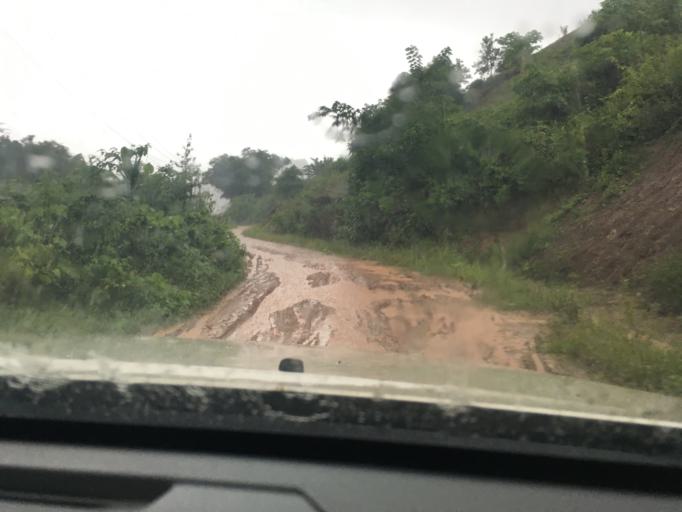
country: LA
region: Oudomxai
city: Muang La
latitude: 21.2252
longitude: 101.9710
